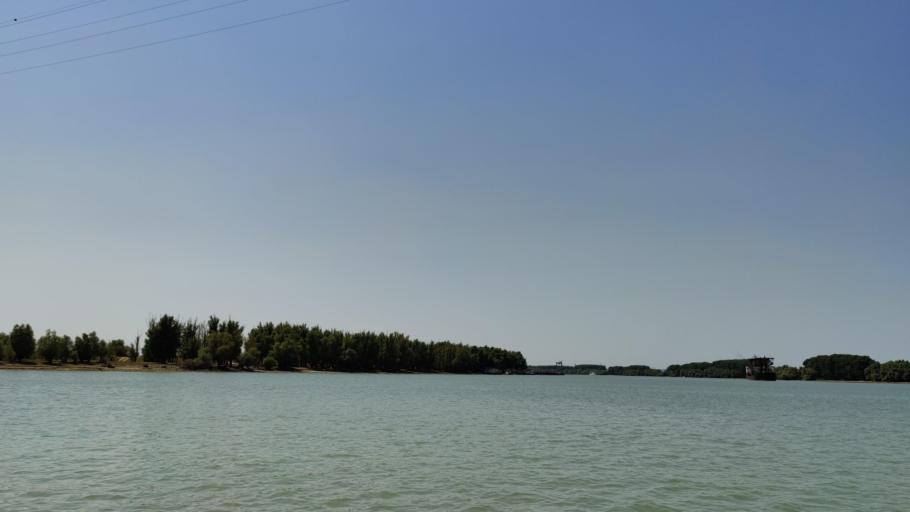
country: RO
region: Tulcea
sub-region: Municipiul Tulcea
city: Tulcea
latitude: 45.2028
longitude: 28.8458
